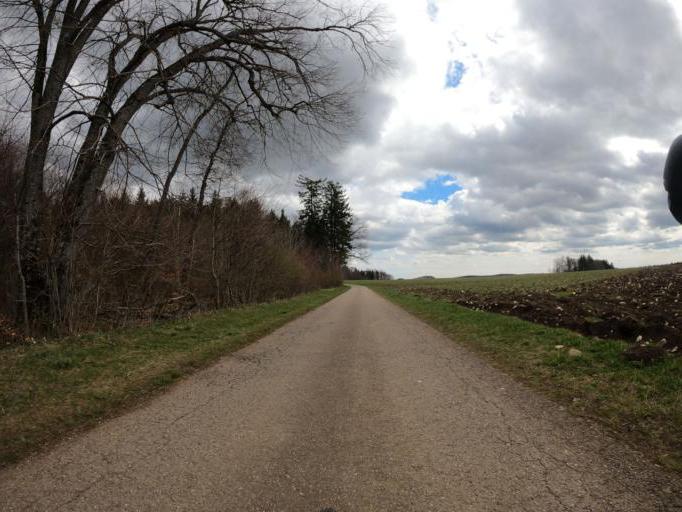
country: DE
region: Baden-Wuerttemberg
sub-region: Tuebingen Region
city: Jungingen
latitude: 48.3605
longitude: 9.0690
